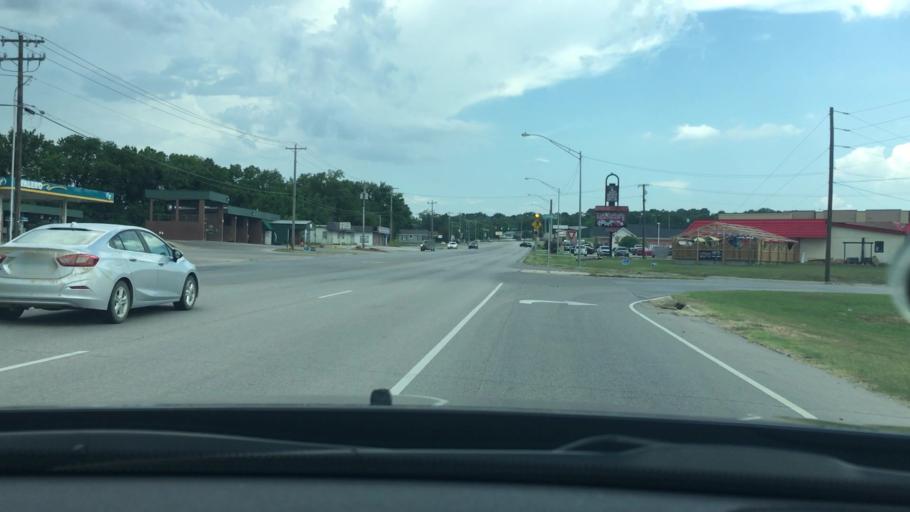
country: US
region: Oklahoma
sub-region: Pontotoc County
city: Ada
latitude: 34.7587
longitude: -96.6612
